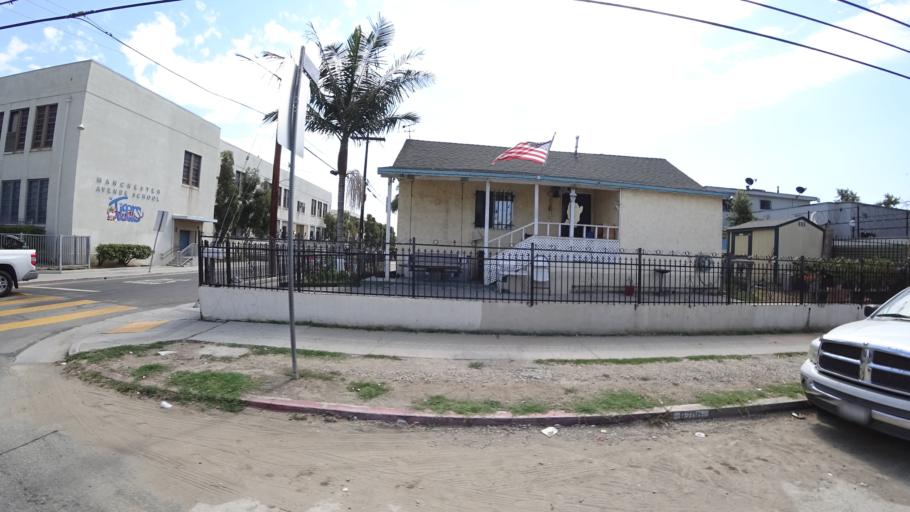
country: US
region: California
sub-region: Los Angeles County
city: Westmont
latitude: 33.9586
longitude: -118.2869
